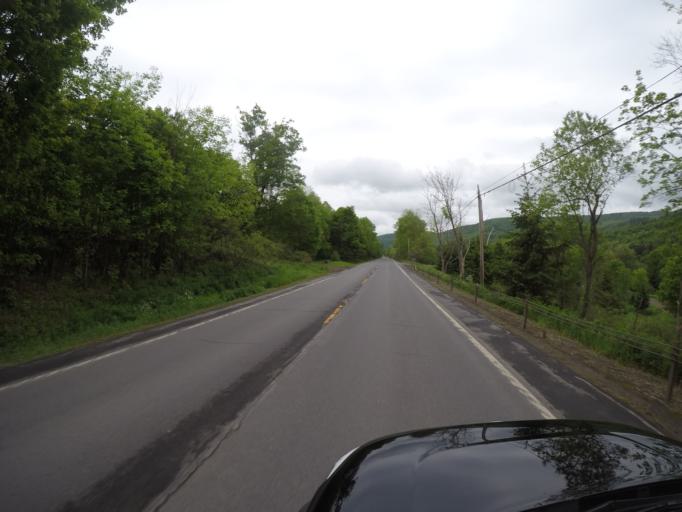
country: US
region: New York
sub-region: Delaware County
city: Delhi
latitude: 42.2552
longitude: -74.9139
